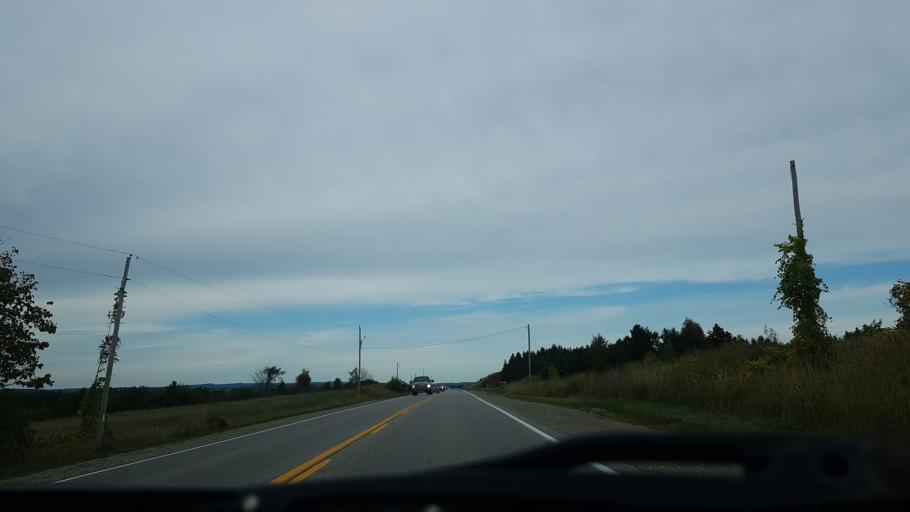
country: CA
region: Ontario
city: Shelburne
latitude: 44.1003
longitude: -80.0234
